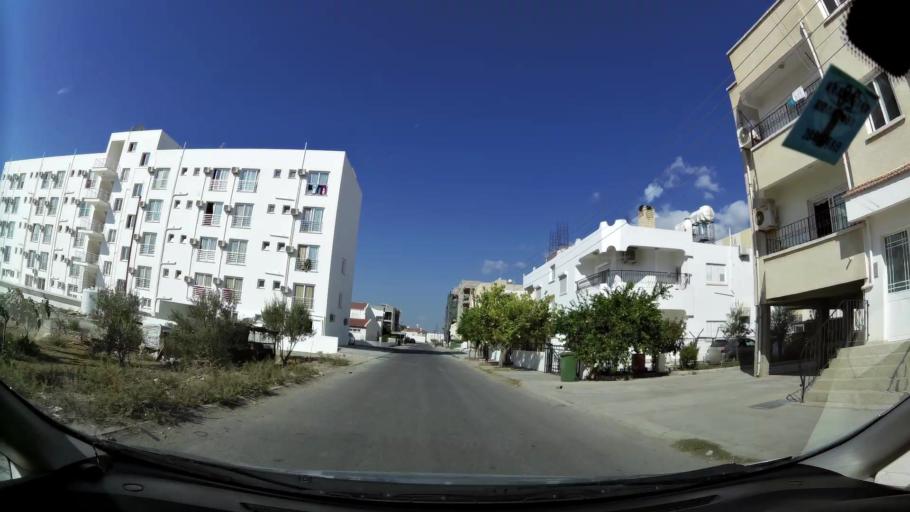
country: CY
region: Lefkosia
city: Nicosia
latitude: 35.2127
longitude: 33.3755
